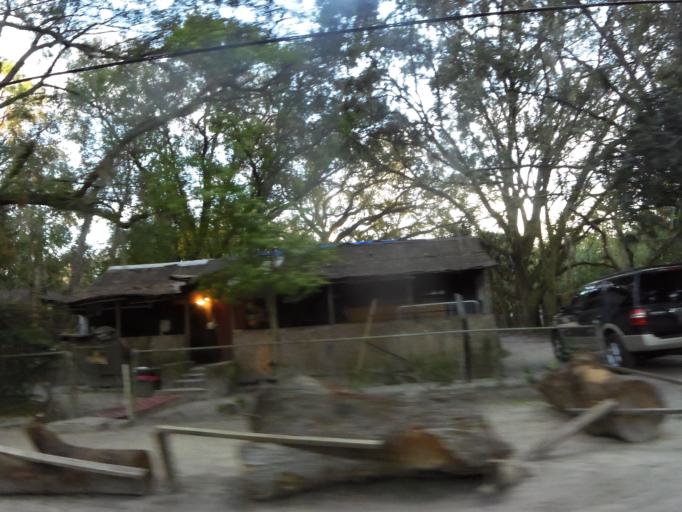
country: US
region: Florida
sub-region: Duval County
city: Jacksonville
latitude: 30.2796
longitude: -81.6417
